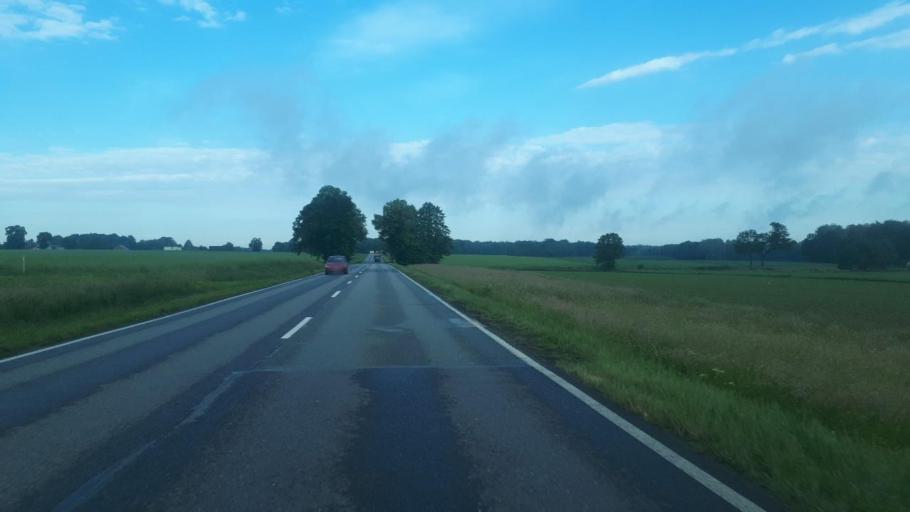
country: PL
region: Silesian Voivodeship
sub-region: Powiat pszczynski
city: Miedzna
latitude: 49.9693
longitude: 19.0385
